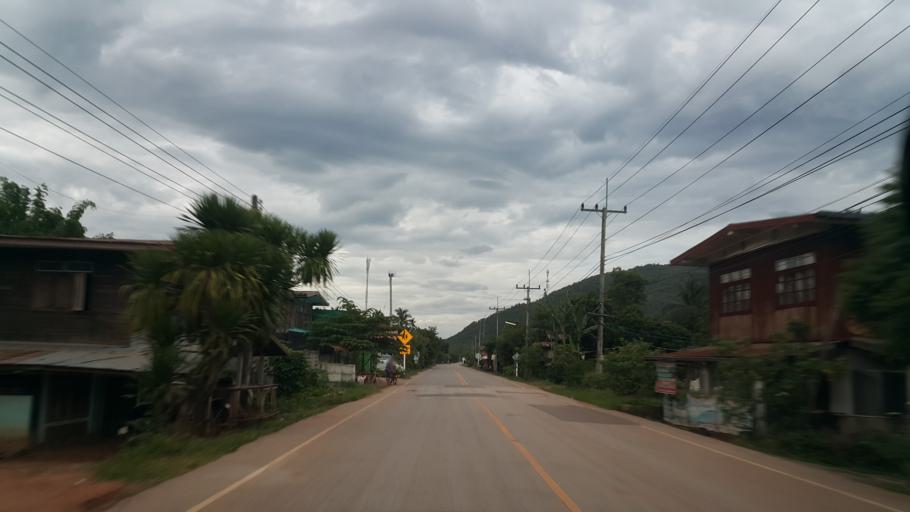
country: TH
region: Loei
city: Na Haeo
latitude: 17.5193
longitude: 101.1779
